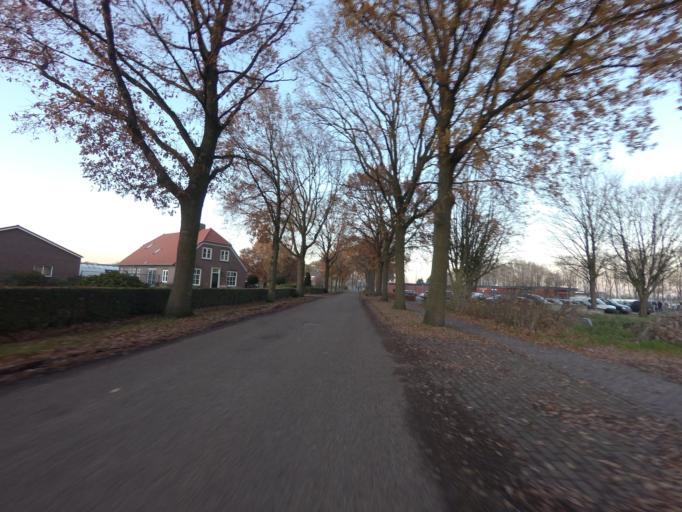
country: NL
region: Gelderland
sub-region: Gemeente Maasdriel
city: Hedel
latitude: 51.7526
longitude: 5.2275
